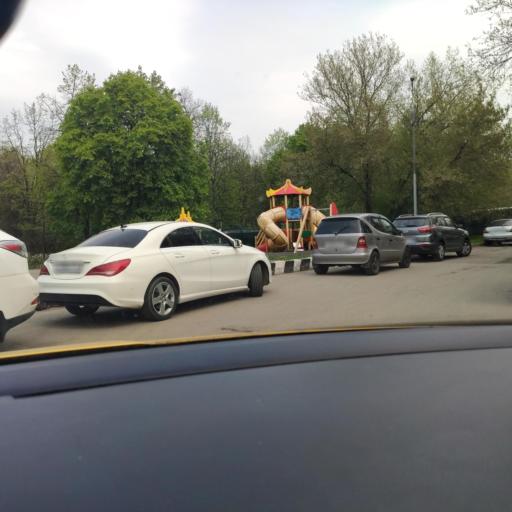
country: RU
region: Moscow
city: Lyublino
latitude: 55.6861
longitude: 37.7583
